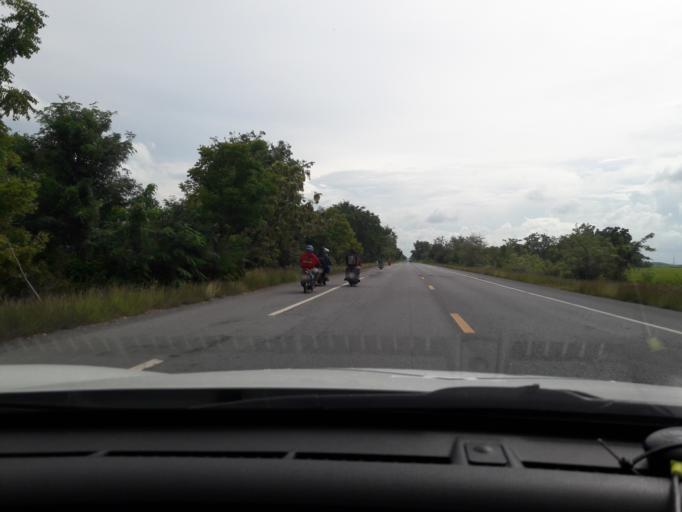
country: TH
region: Nakhon Sawan
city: Phai Sali
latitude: 15.5374
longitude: 100.5513
